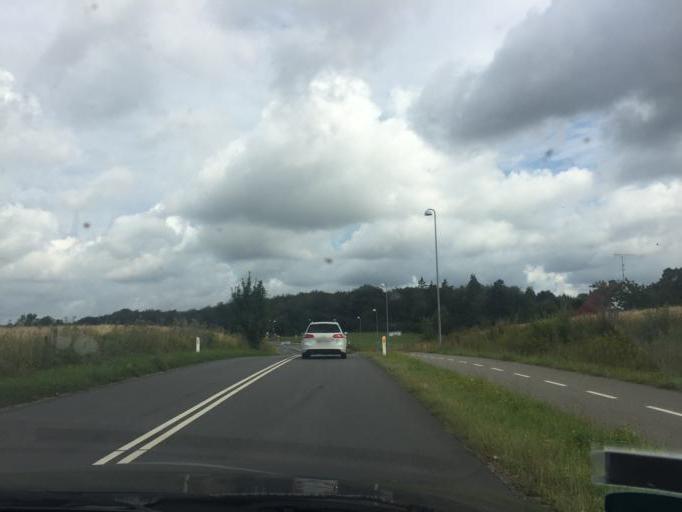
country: DK
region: Capital Region
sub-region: Allerod Kommune
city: Lillerod
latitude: 55.9001
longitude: 12.3448
